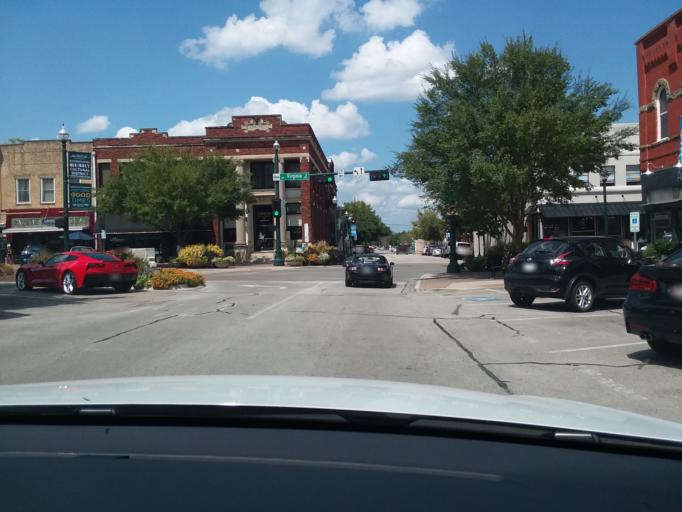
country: US
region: Texas
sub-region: Collin County
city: McKinney
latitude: 33.1977
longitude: -96.6152
